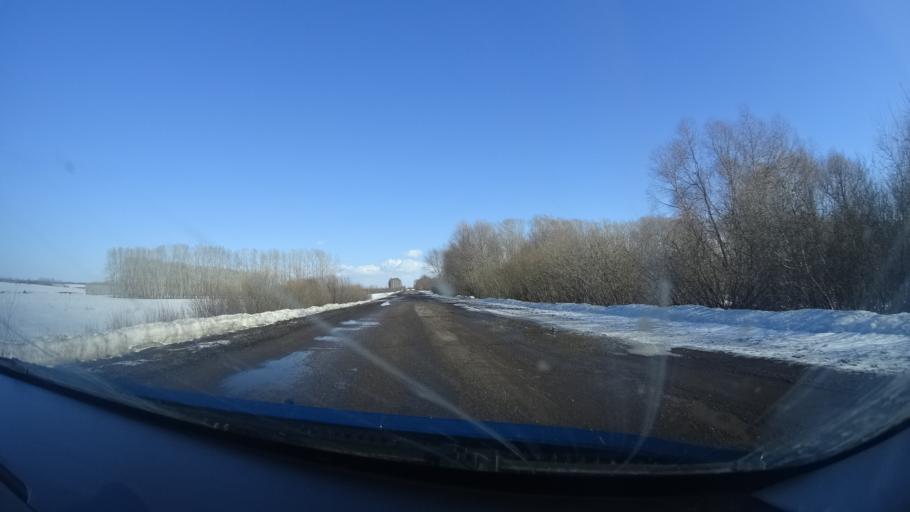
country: RU
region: Bashkortostan
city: Chishmy
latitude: 54.5890
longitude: 55.2727
